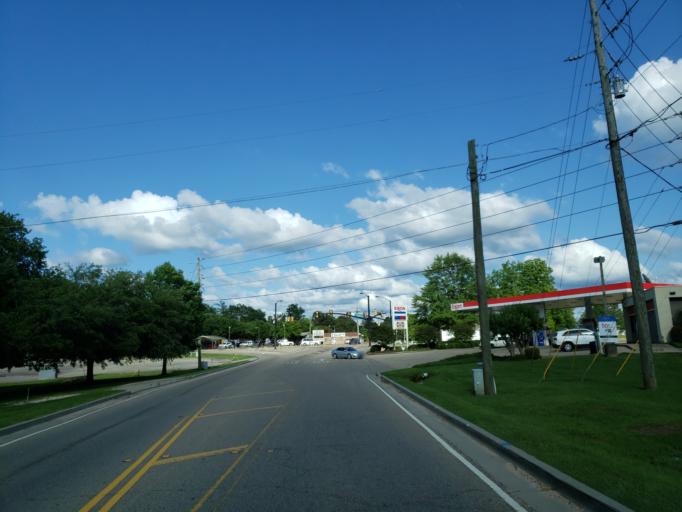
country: US
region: Mississippi
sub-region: Lamar County
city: West Hattiesburg
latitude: 31.2862
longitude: -89.4156
